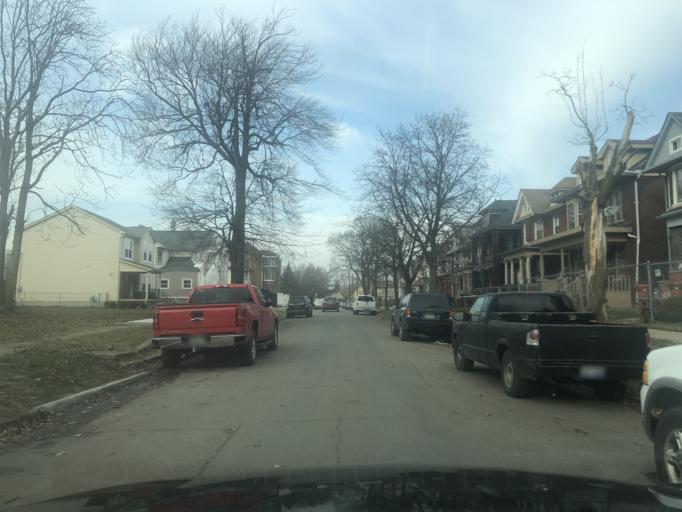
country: US
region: Michigan
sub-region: Wayne County
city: River Rouge
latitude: 42.3197
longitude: -83.1018
